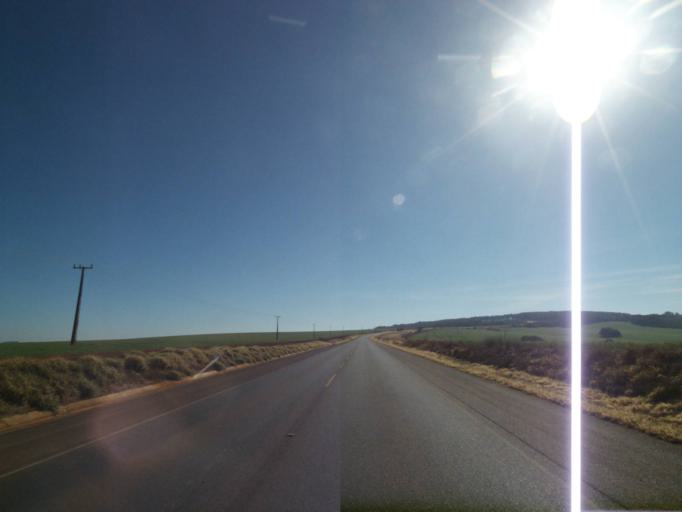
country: BR
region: Parana
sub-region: Tibagi
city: Tibagi
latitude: -24.4440
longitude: -50.4233
